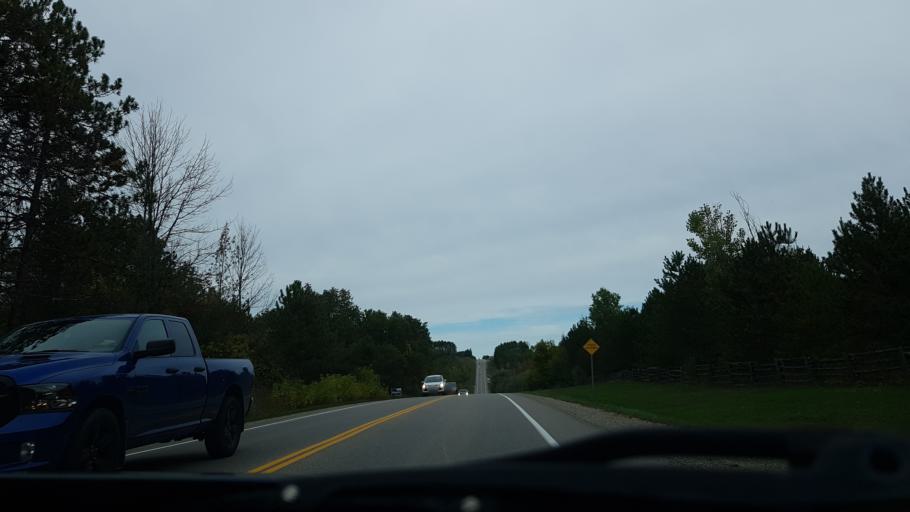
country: CA
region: Ontario
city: Orangeville
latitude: 44.0174
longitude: -80.0029
